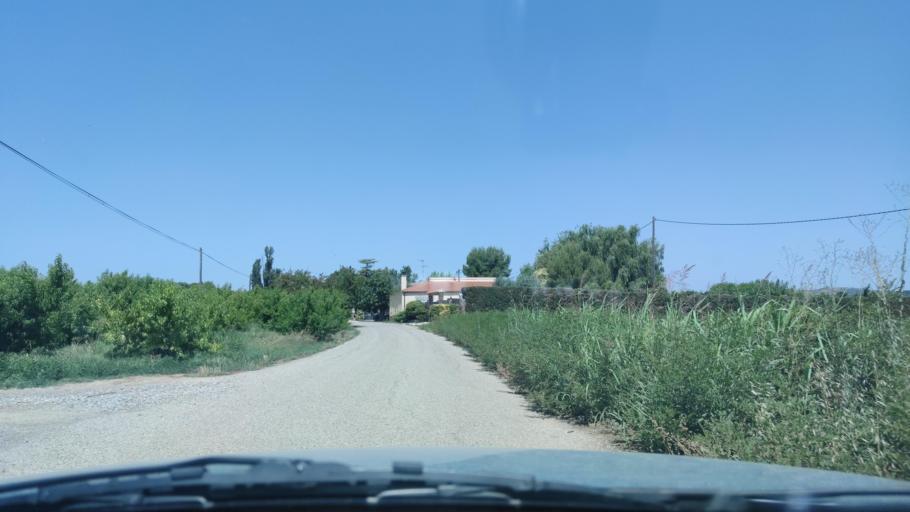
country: ES
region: Catalonia
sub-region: Provincia de Lleida
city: Torrefarrera
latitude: 41.6501
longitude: 0.5936
